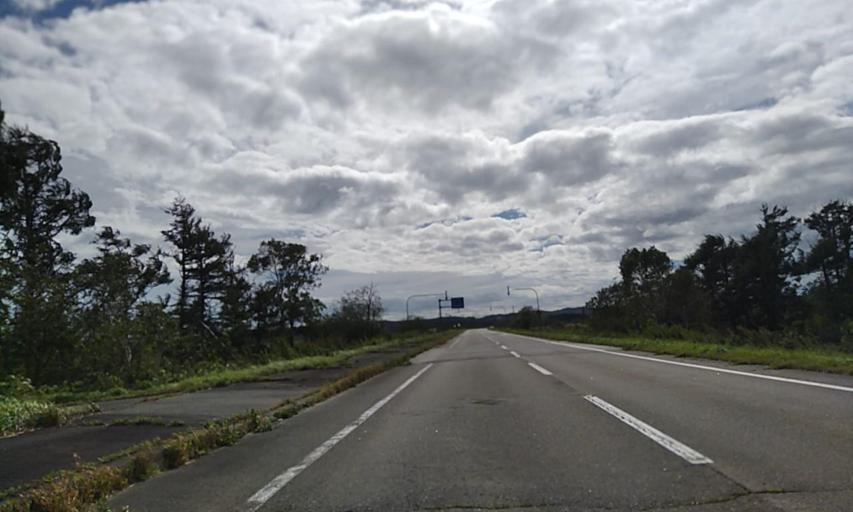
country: JP
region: Hokkaido
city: Obihiro
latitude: 42.7144
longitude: 143.6376
